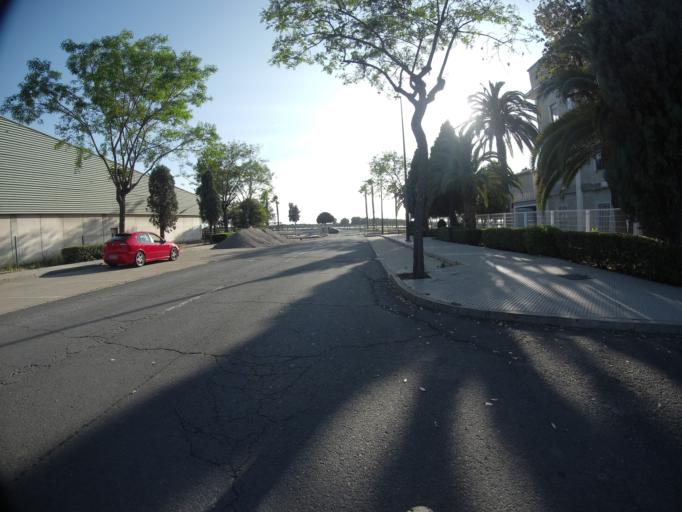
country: ES
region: Andalusia
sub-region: Provincia de Huelva
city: Huelva
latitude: 37.2391
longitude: -6.9534
